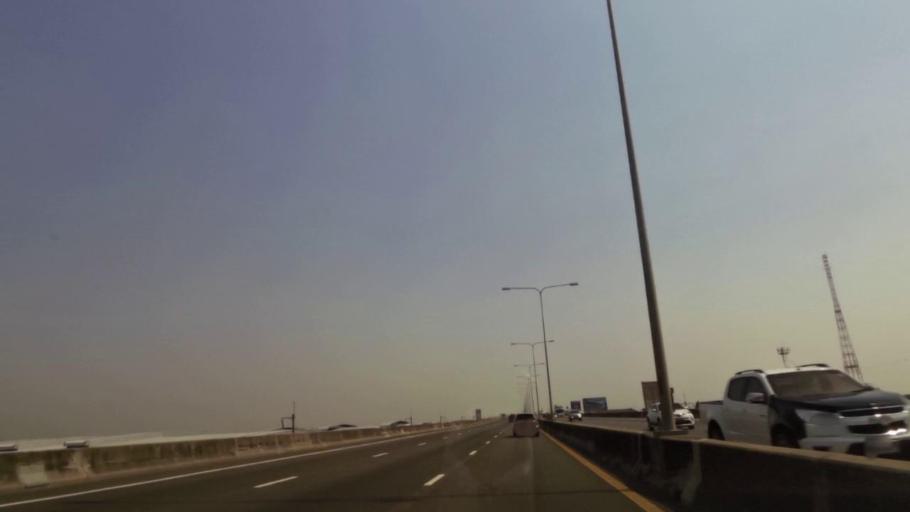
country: TH
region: Samut Prakan
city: Bang Sao Thong
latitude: 13.5893
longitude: 100.8342
